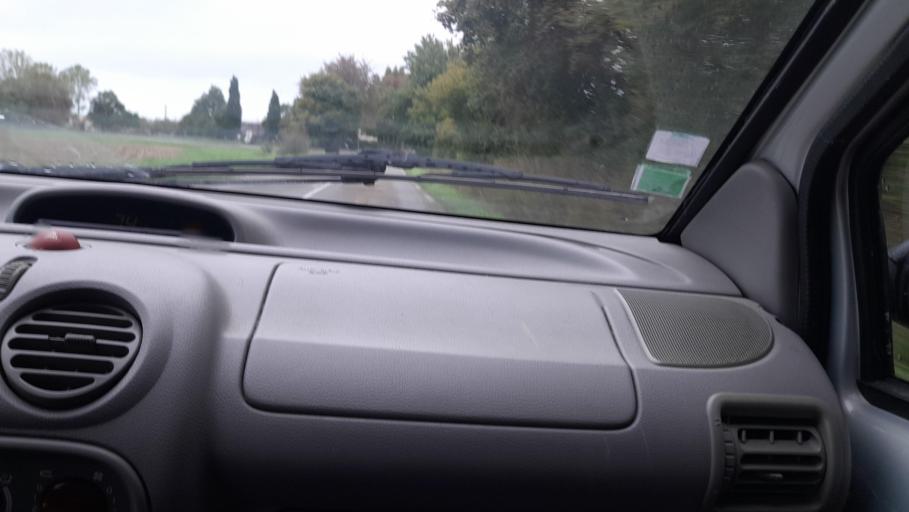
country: FR
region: Pays de la Loire
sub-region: Departement de la Mayenne
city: Ballots
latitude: 47.8999
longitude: -1.1099
